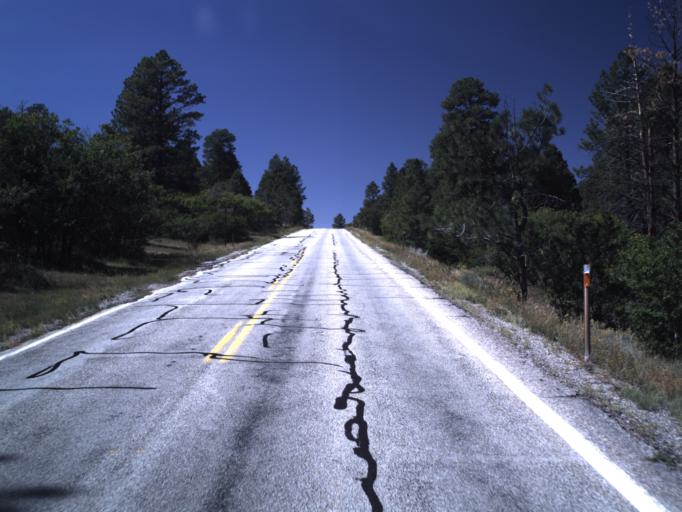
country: US
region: Utah
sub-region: Grand County
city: Moab
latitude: 38.3441
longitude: -109.1993
